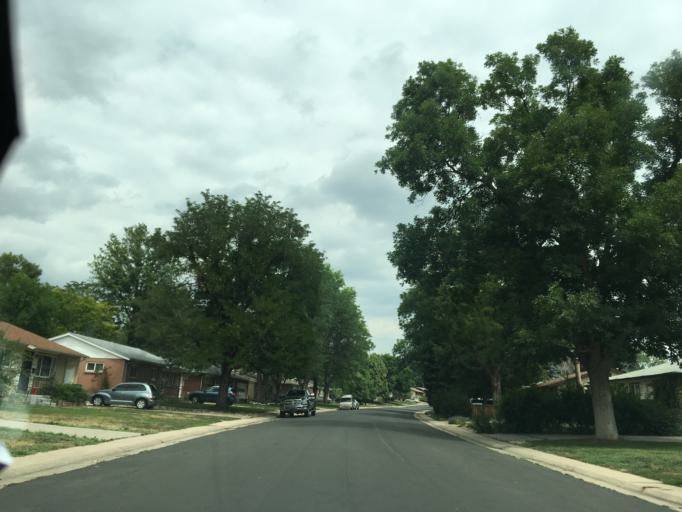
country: US
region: Colorado
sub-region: Arapahoe County
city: Sheridan
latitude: 39.6587
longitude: -105.0476
